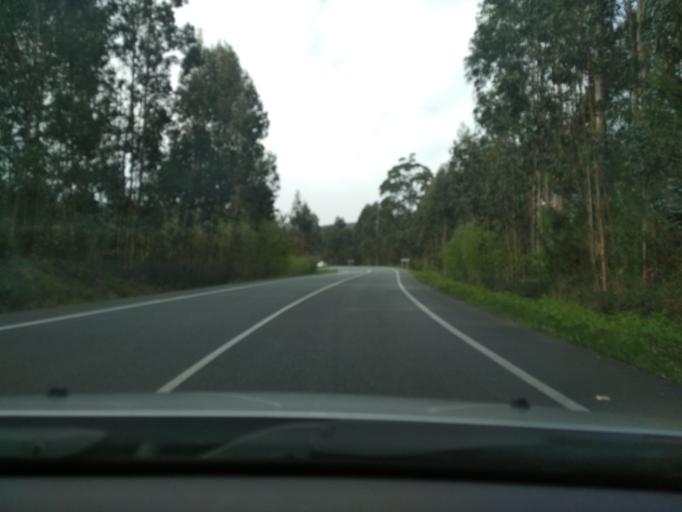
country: ES
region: Galicia
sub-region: Provincia de Pontevedra
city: Catoira
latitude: 42.6605
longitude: -8.7025
